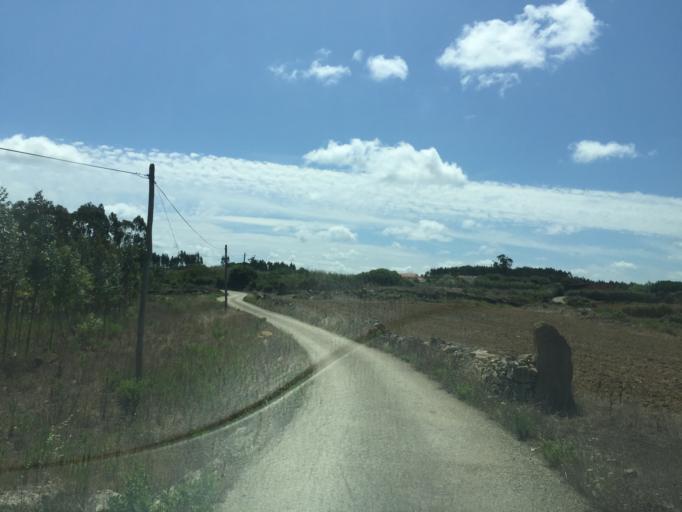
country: PT
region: Leiria
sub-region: Bombarral
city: Bombarral
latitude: 39.2944
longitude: -9.2273
